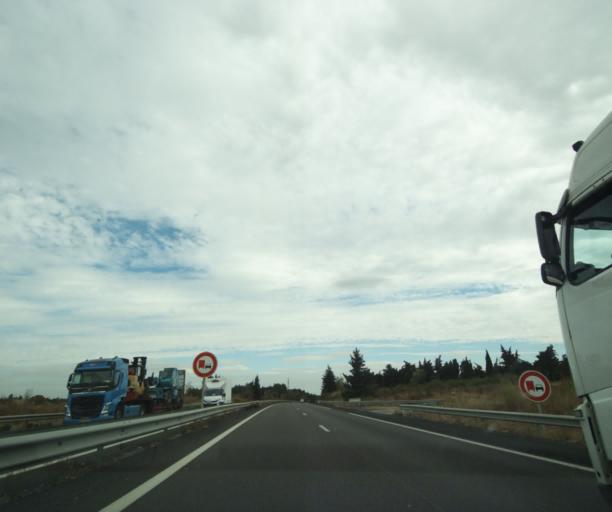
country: FR
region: Languedoc-Roussillon
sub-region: Departement du Gard
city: Garons
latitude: 43.7409
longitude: 4.4535
